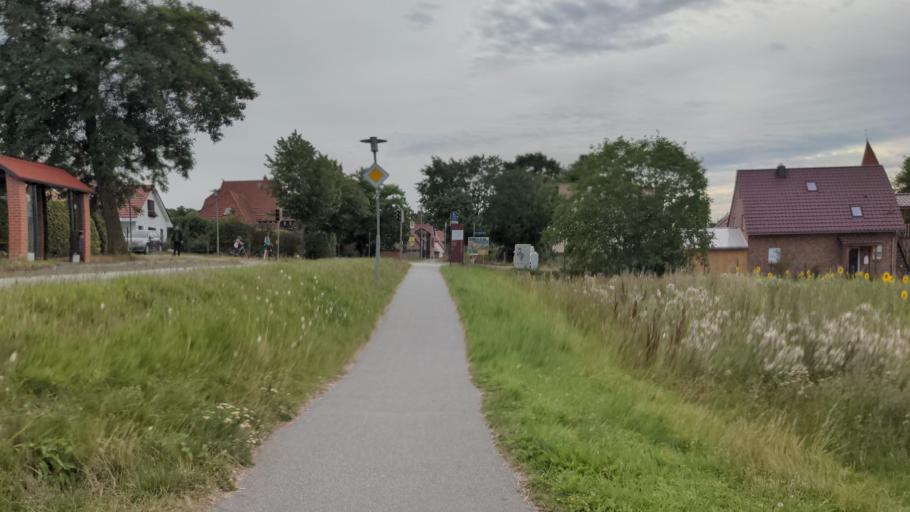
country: DE
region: Mecklenburg-Vorpommern
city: Klutz
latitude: 53.9675
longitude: 11.1705
